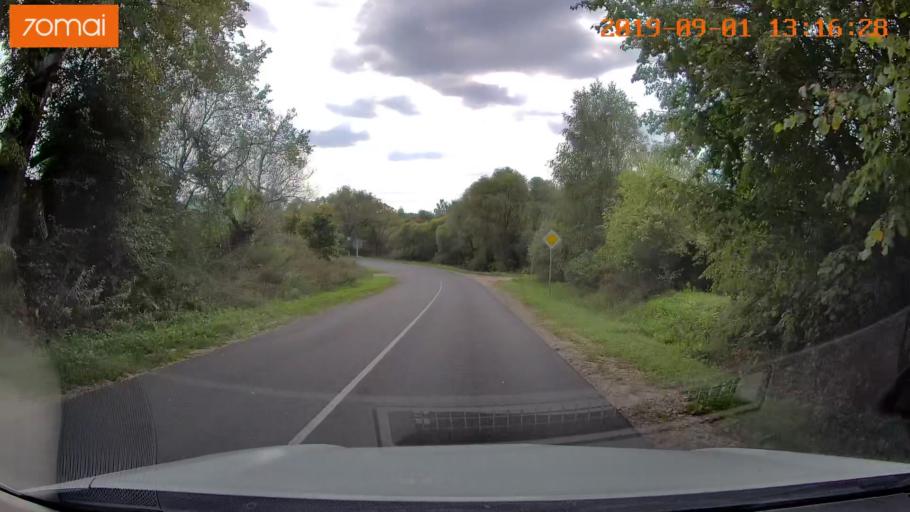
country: RU
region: Kaluga
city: Maloyaroslavets
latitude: 54.9445
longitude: 36.4582
